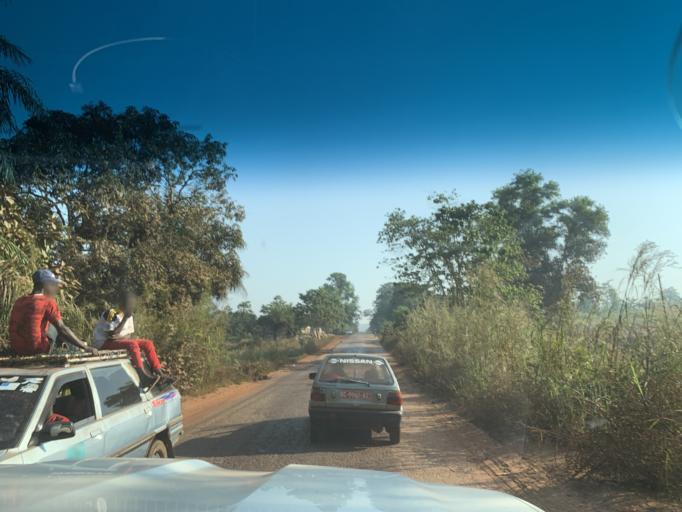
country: GN
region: Kindia
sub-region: Coyah
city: Coyah
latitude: 9.8092
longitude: -13.2748
